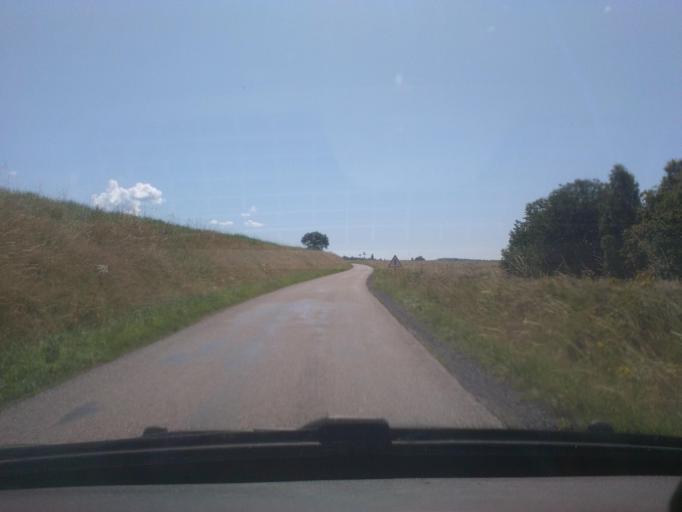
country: FR
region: Lorraine
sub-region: Departement des Vosges
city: Etival-Clairefontaine
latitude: 48.3492
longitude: 6.8624
